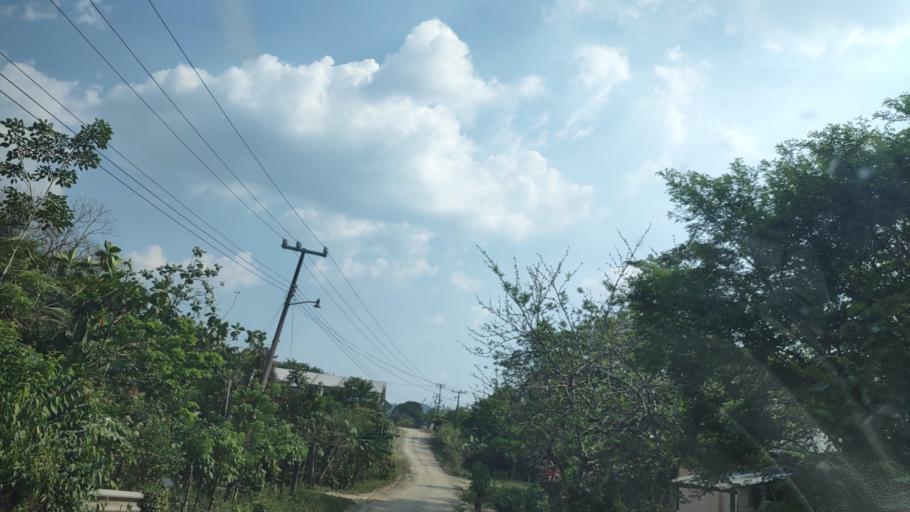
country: MX
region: Chiapas
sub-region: Tecpatan
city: Raudales Malpaso
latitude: 17.3254
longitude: -93.7457
